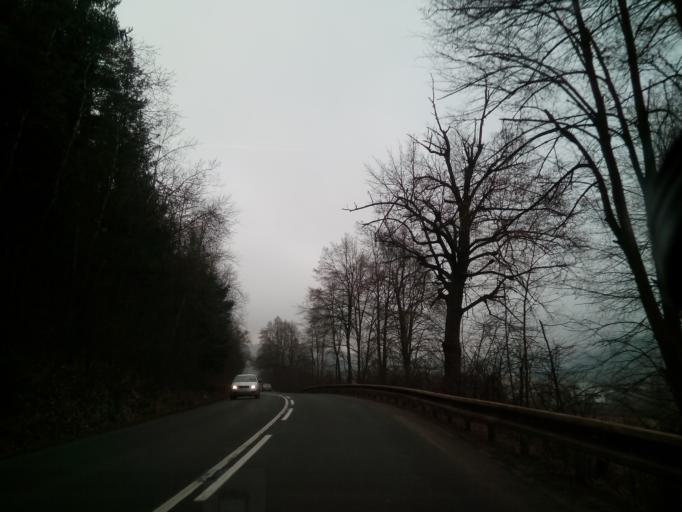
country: SK
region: Kosicky
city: Krompachy
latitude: 48.9255
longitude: 20.9069
